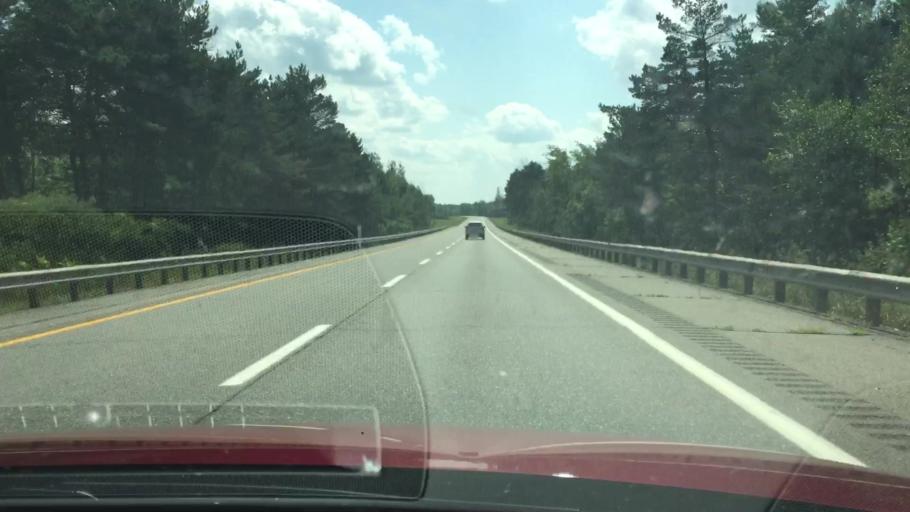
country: US
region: Maine
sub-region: Penobscot County
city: Lincoln
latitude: 45.3923
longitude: -68.6027
